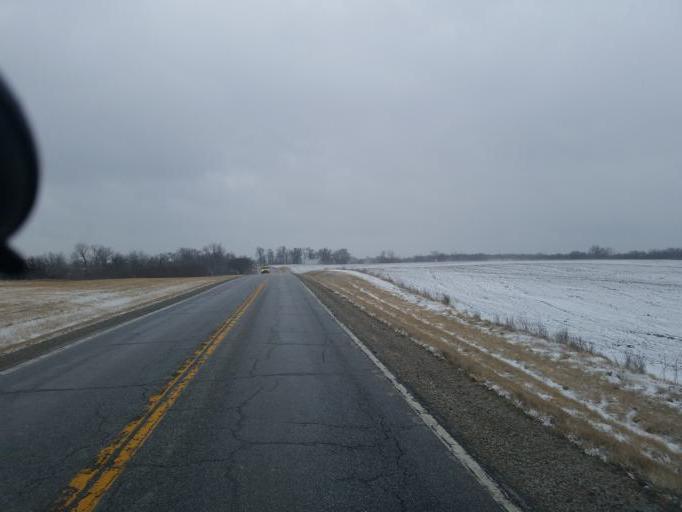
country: US
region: Missouri
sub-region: Putnam County
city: Unionville
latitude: 40.5066
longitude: -93.0096
